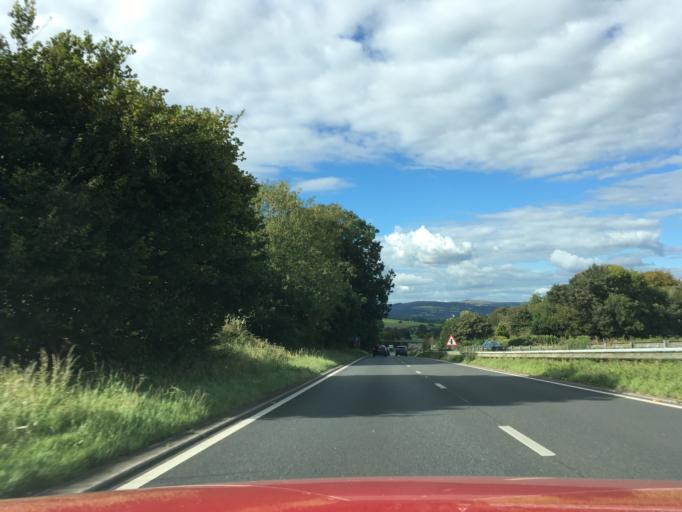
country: GB
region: England
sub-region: Devon
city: Buckfastleigh
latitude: 50.4546
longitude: -3.7908
